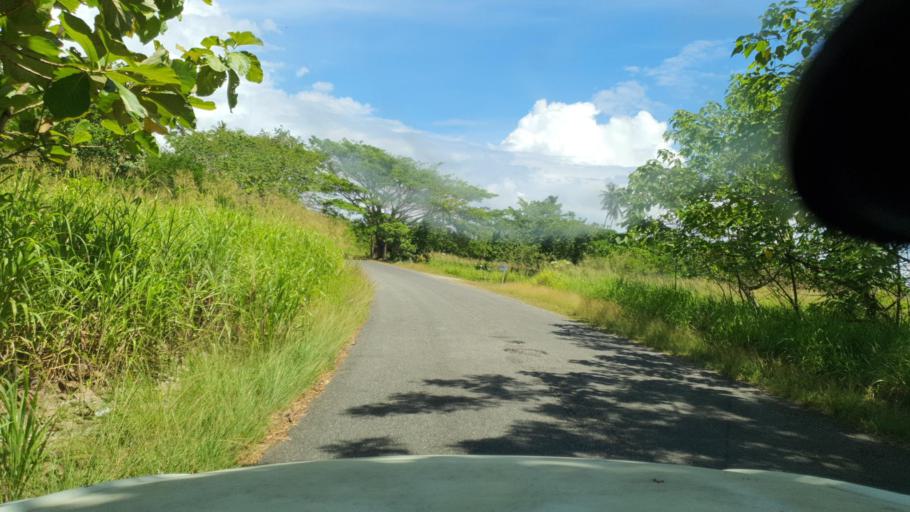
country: SB
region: Guadalcanal
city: Honiara
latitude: -9.3571
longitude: 159.8485
